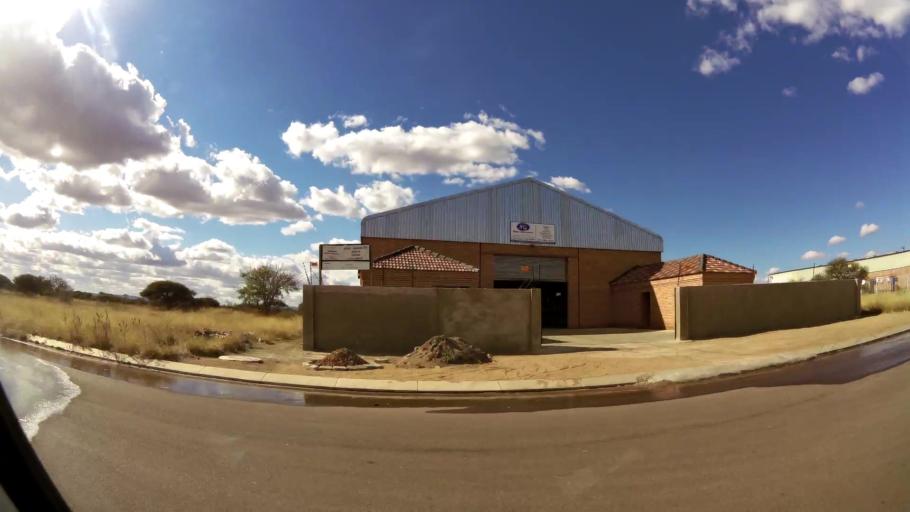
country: ZA
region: Limpopo
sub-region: Capricorn District Municipality
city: Polokwane
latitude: -23.8643
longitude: 29.4801
